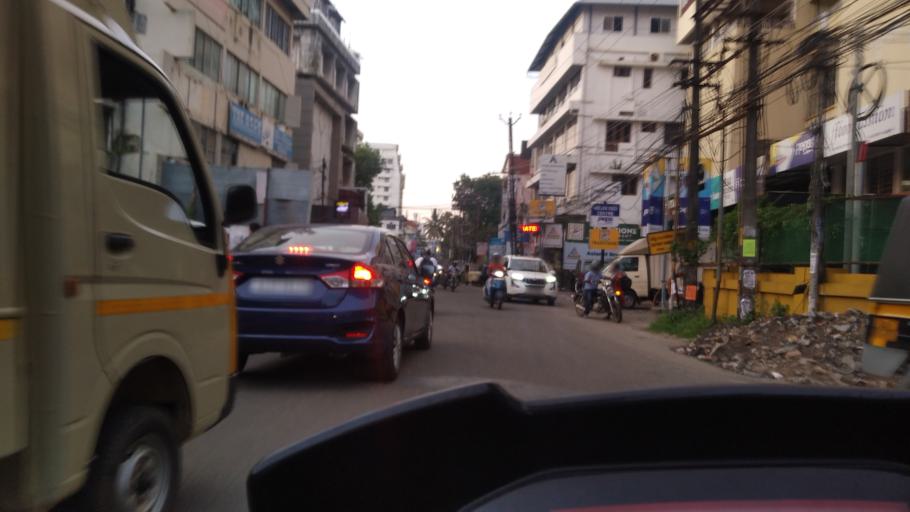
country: IN
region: Kerala
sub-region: Ernakulam
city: Cochin
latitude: 9.9810
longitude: 76.2846
